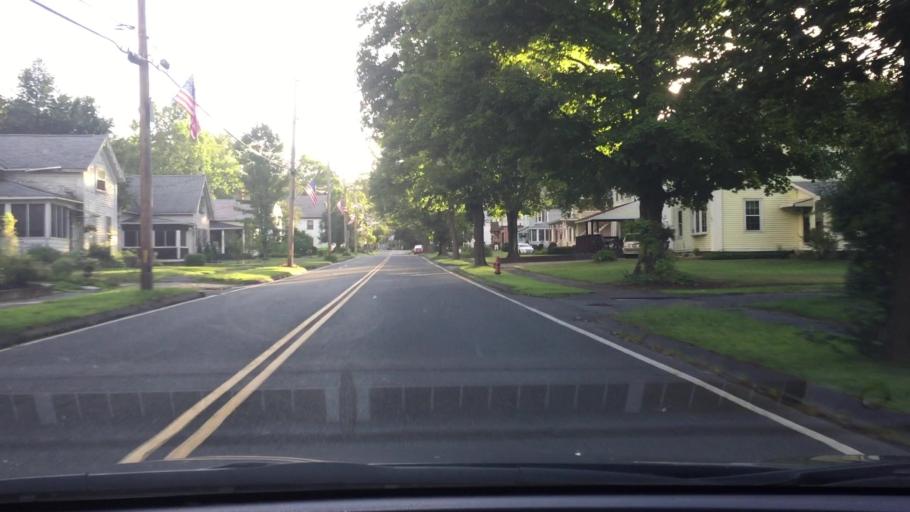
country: US
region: Massachusetts
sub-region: Hampden County
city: Granville
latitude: 42.1898
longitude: -72.8546
